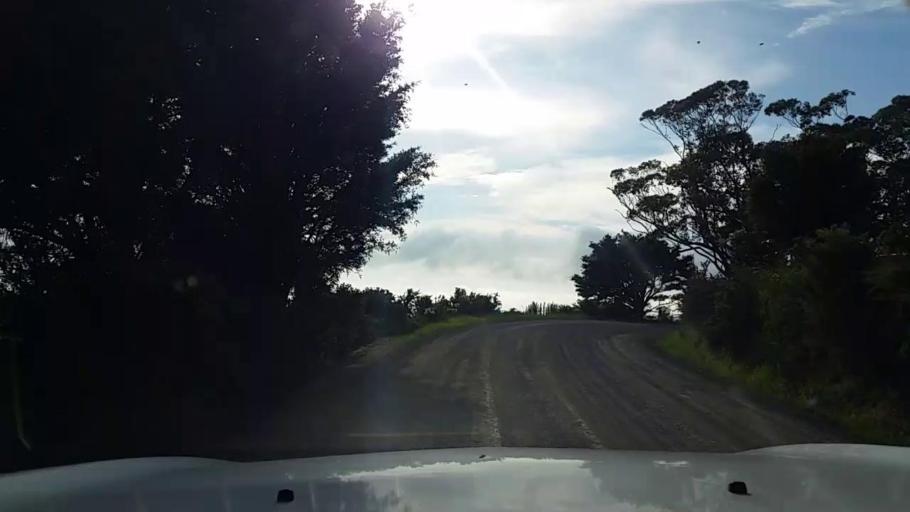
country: NZ
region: Northland
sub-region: Whangarei
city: Maungatapere
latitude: -35.6689
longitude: 174.1752
